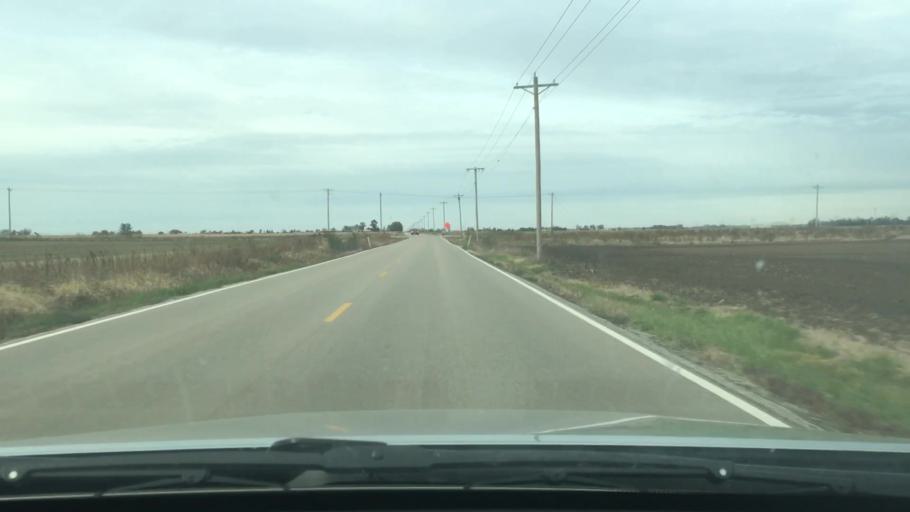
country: US
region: Kansas
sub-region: Sedgwick County
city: Maize
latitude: 37.7635
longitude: -97.4992
